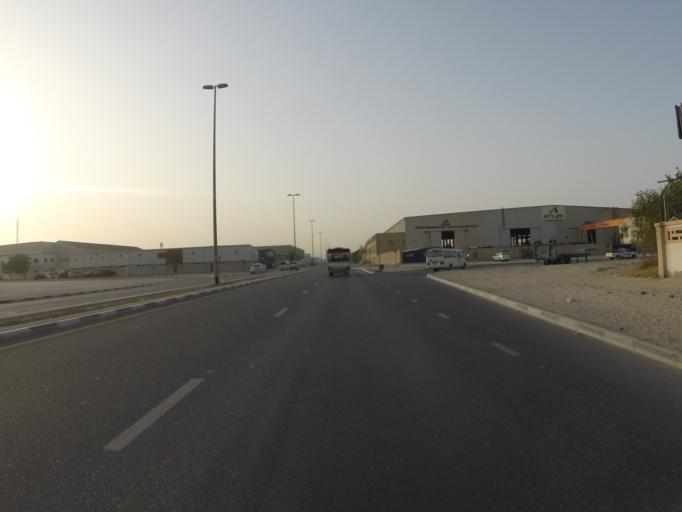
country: AE
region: Dubai
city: Dubai
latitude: 25.1346
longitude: 55.2254
